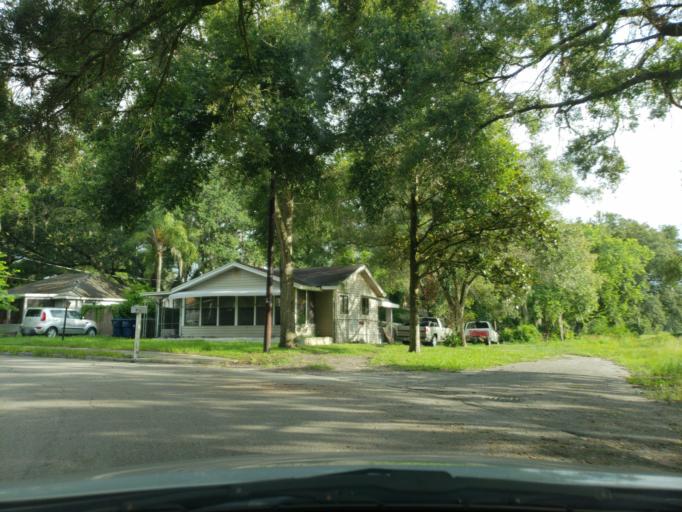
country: US
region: Florida
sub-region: Hillsborough County
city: Temple Terrace
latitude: 28.0073
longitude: -82.4388
